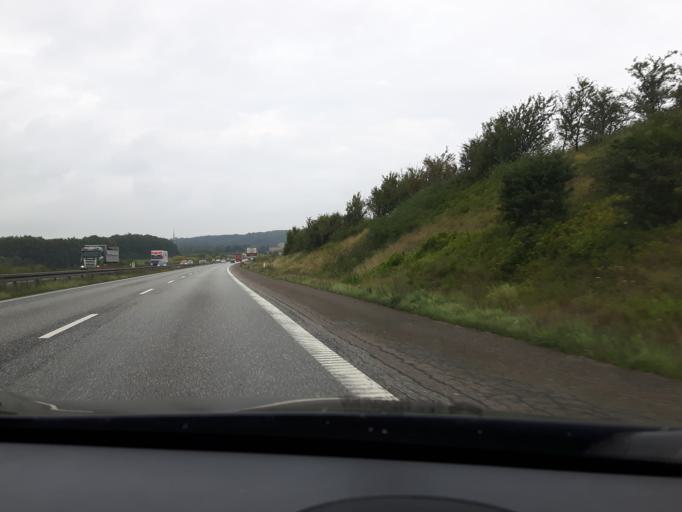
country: DK
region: North Denmark
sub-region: Mariagerfjord Kommune
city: Hobro
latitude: 56.6071
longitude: 9.7437
